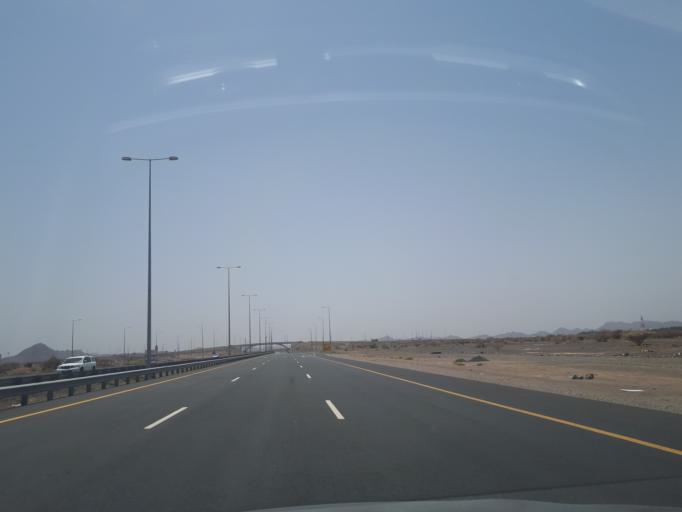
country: OM
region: Ash Sharqiyah
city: Ibra'
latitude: 22.7732
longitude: 58.5159
